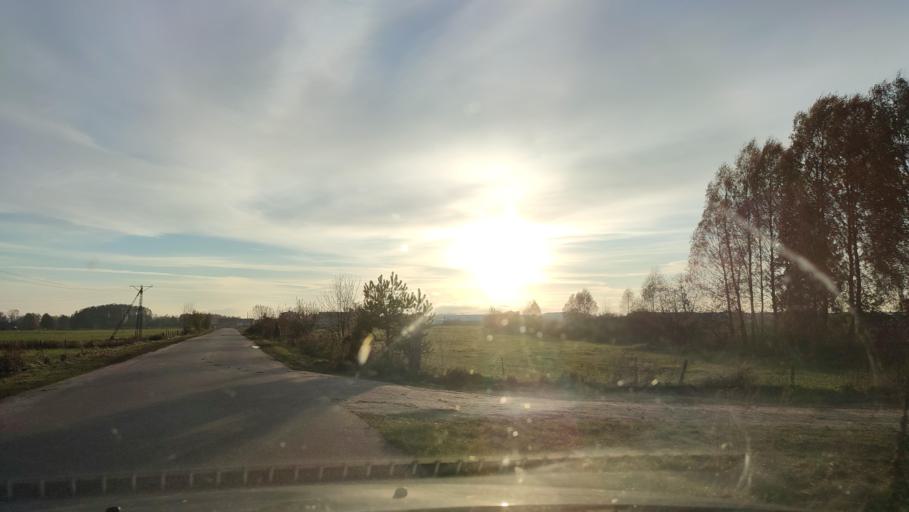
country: PL
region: Masovian Voivodeship
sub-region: Powiat mlawski
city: Dzierzgowo
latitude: 53.2853
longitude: 20.6562
